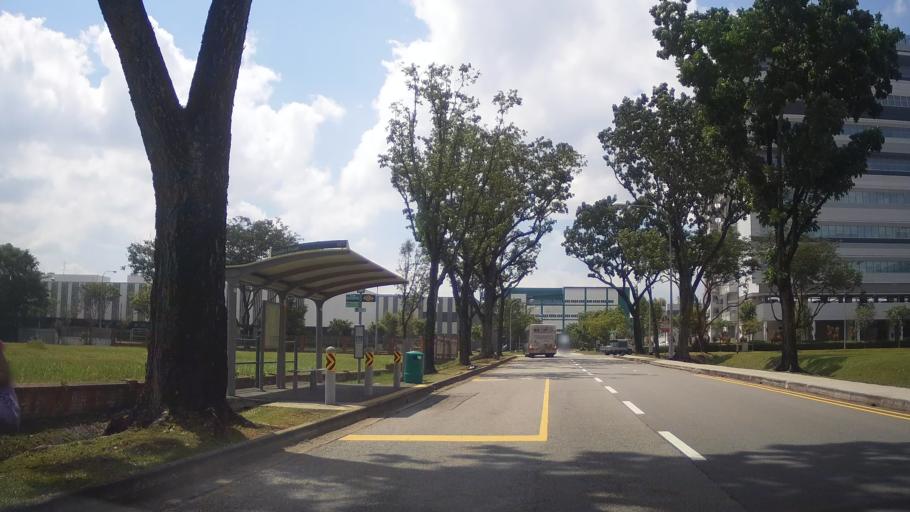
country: SG
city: Singapore
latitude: 1.3268
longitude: 103.7109
